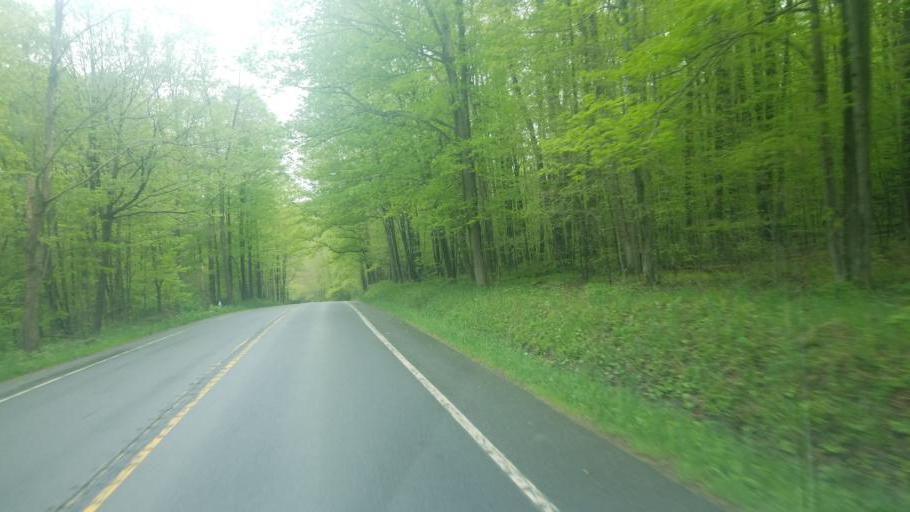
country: US
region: Pennsylvania
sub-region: McKean County
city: Kane
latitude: 41.6036
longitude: -78.8421
